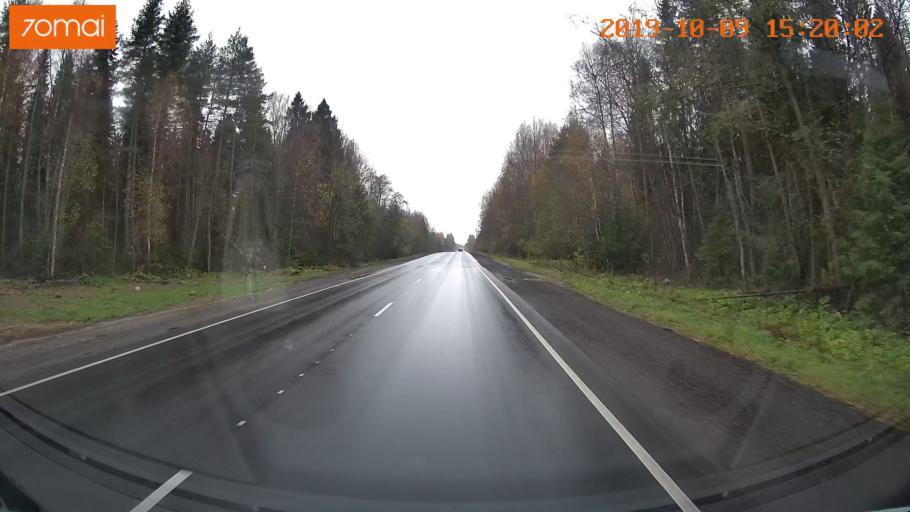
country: RU
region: Kostroma
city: Susanino
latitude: 58.0690
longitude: 41.5454
